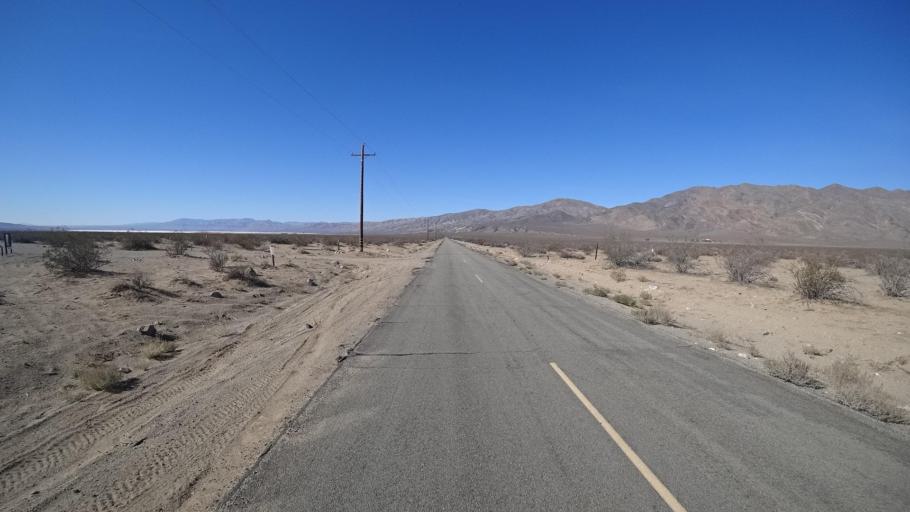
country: US
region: California
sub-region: Kern County
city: China Lake Acres
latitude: 35.3898
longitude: -117.7723
